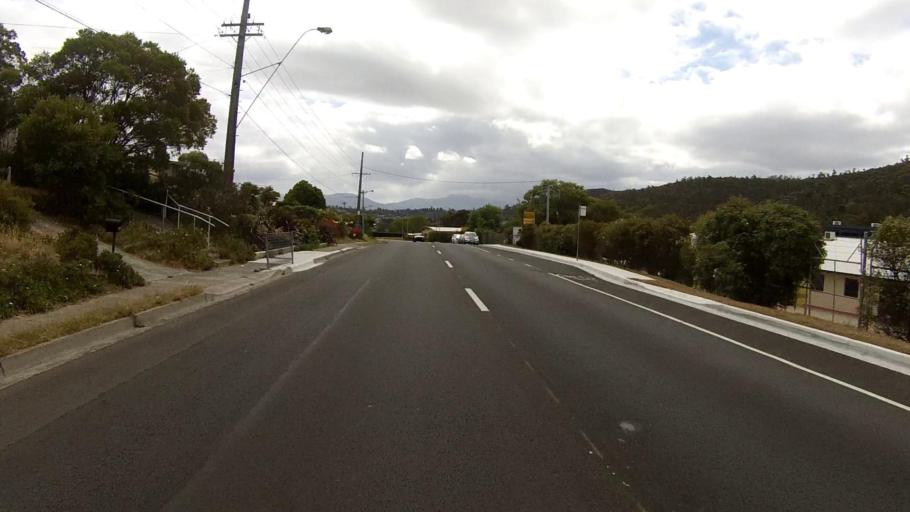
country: AU
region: Tasmania
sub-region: Clarence
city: Warrane
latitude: -42.8562
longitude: 147.4008
